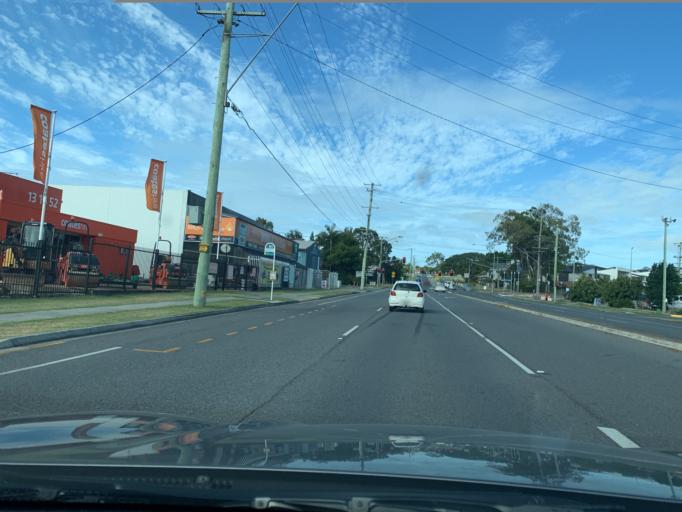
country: AU
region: Queensland
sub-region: Brisbane
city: Wynnum West
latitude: -27.4673
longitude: 153.1533
